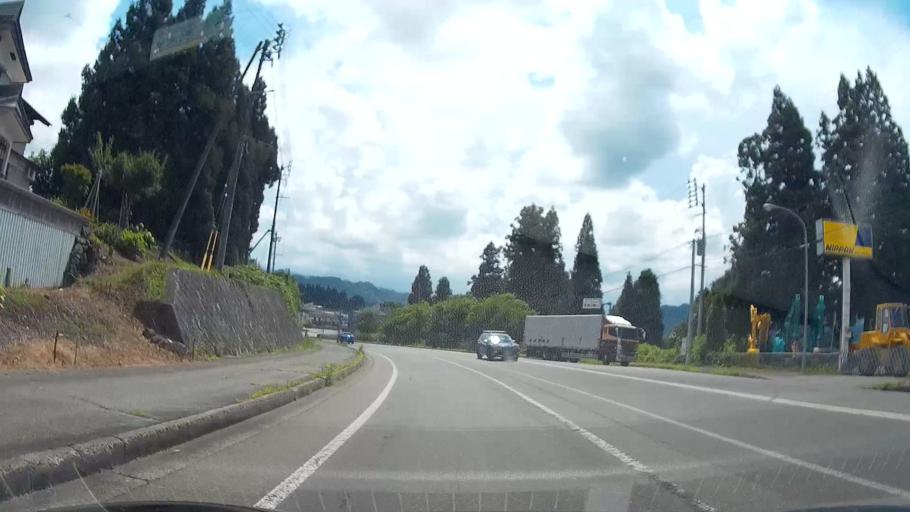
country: JP
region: Niigata
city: Tokamachi
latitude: 37.0288
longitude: 138.6650
